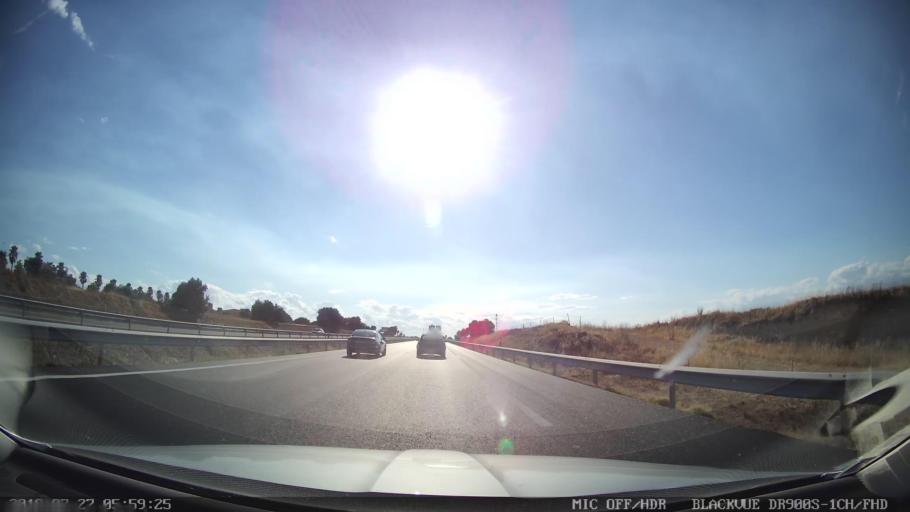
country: ES
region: Castille-La Mancha
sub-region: Province of Toledo
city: Herreruela de Oropesa
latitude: 39.9015
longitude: -5.2683
